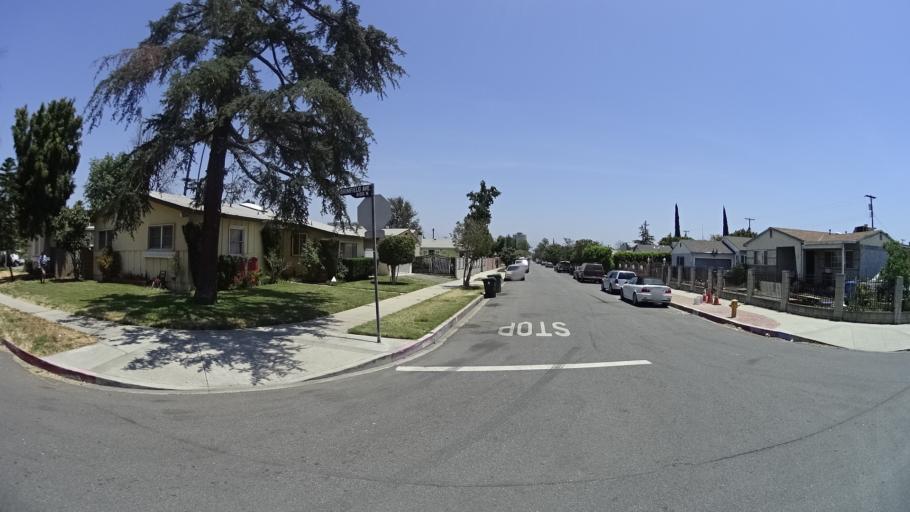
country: US
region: California
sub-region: Los Angeles County
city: Van Nuys
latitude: 34.2193
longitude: -118.4586
